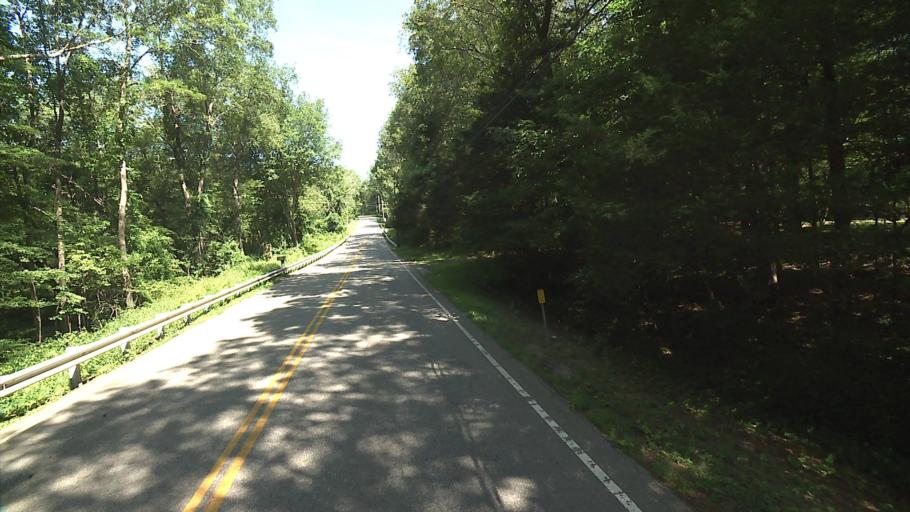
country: US
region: Connecticut
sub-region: New London County
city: Baltic
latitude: 41.6387
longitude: -72.0868
